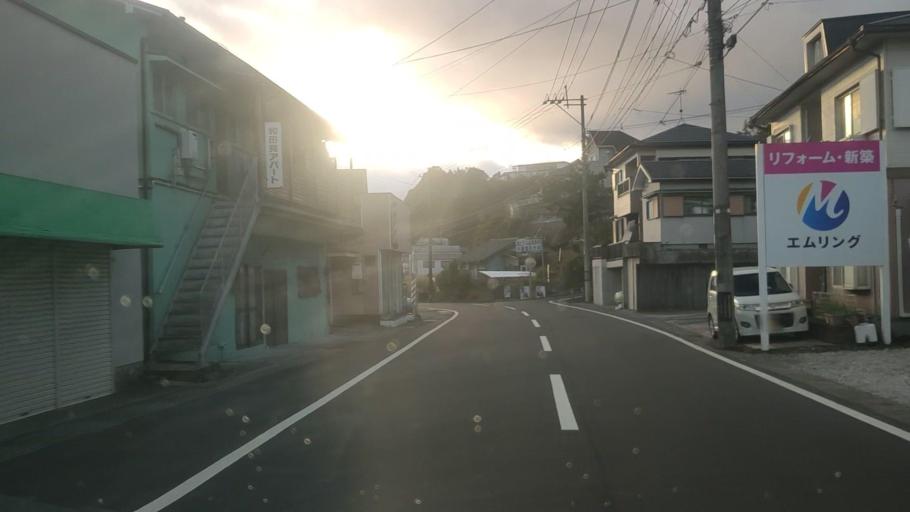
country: JP
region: Kagoshima
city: Kagoshima-shi
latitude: 31.6221
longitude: 130.5402
